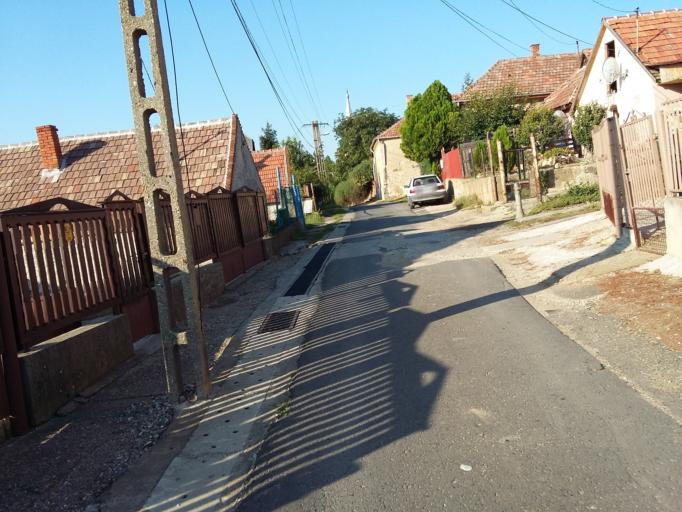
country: HU
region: Borsod-Abauj-Zemplen
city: Bekecs
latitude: 48.1540
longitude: 21.1747
